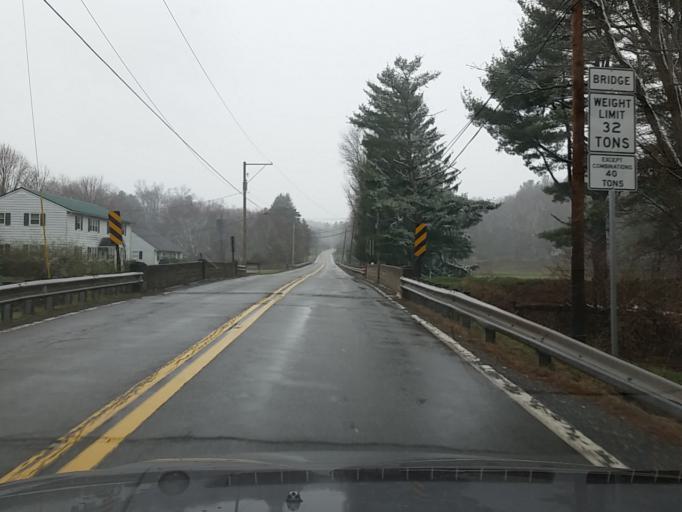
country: US
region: Pennsylvania
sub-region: Luzerne County
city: East Berwick
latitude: 41.1924
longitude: -76.2713
